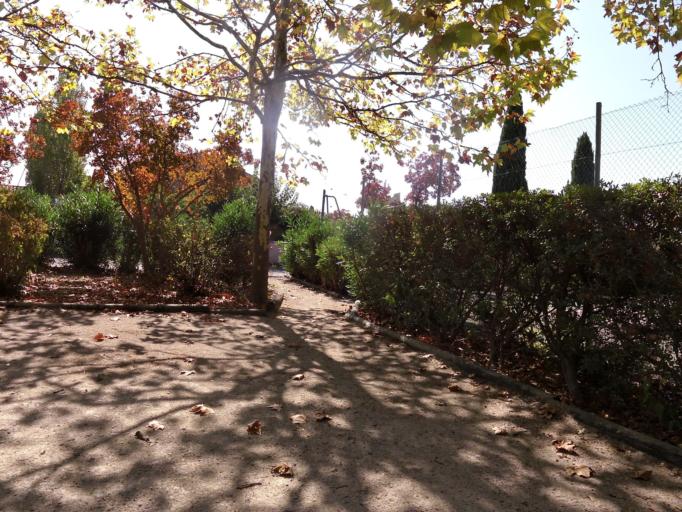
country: FR
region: Languedoc-Roussillon
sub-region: Departement du Gard
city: Calvisson
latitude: 43.7878
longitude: 4.1995
